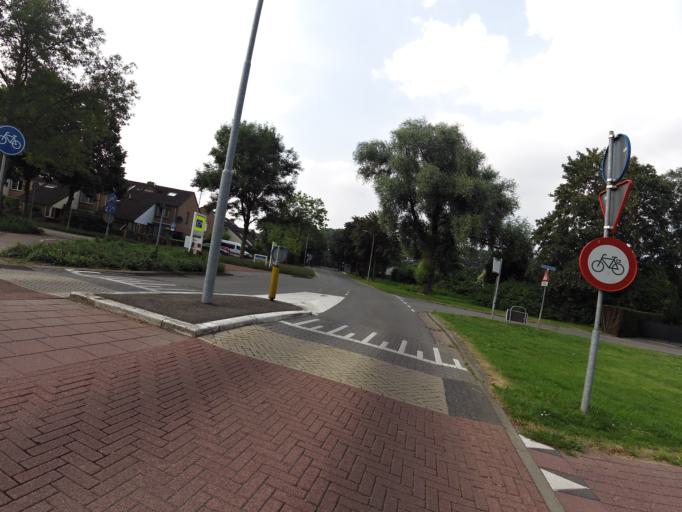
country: NL
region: Gelderland
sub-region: Gemeente Doesburg
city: Doesburg
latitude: 52.0019
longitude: 6.1340
